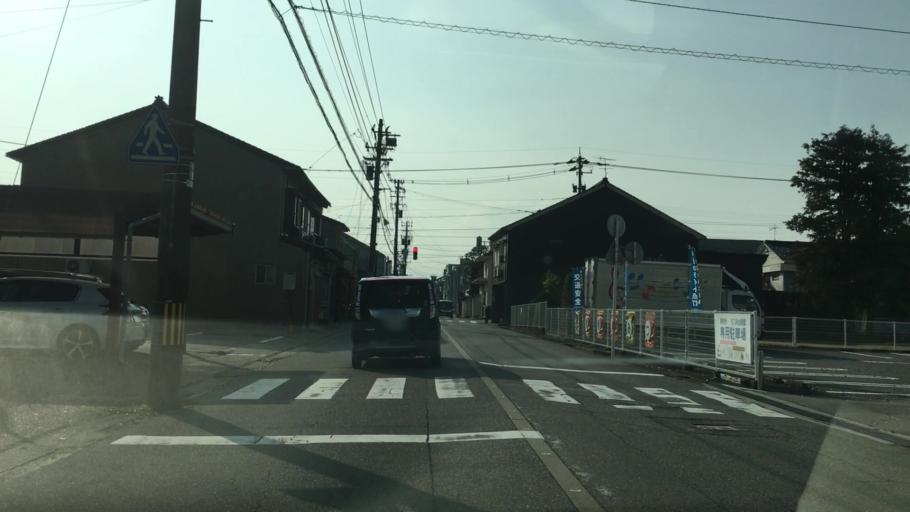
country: JP
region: Toyama
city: Kamiichi
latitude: 36.6660
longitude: 137.3171
